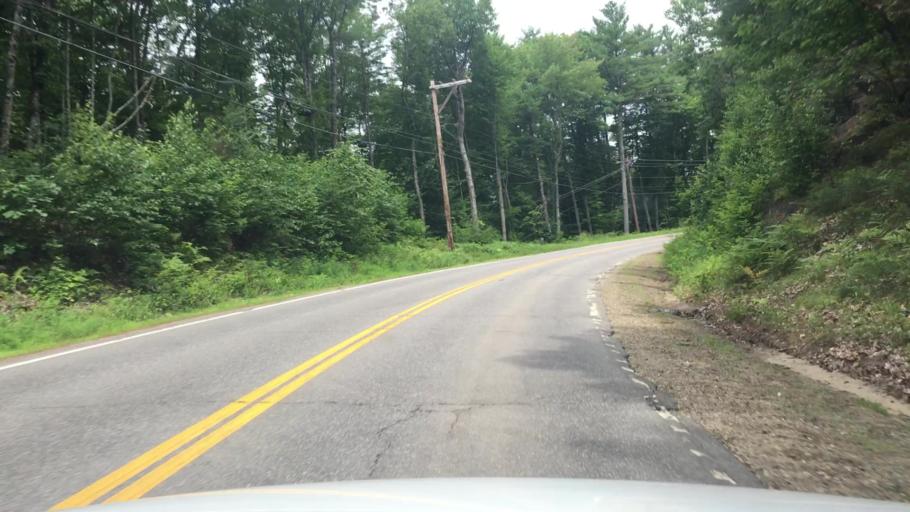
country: US
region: New Hampshire
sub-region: Grafton County
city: Plymouth
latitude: 43.7634
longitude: -71.6746
